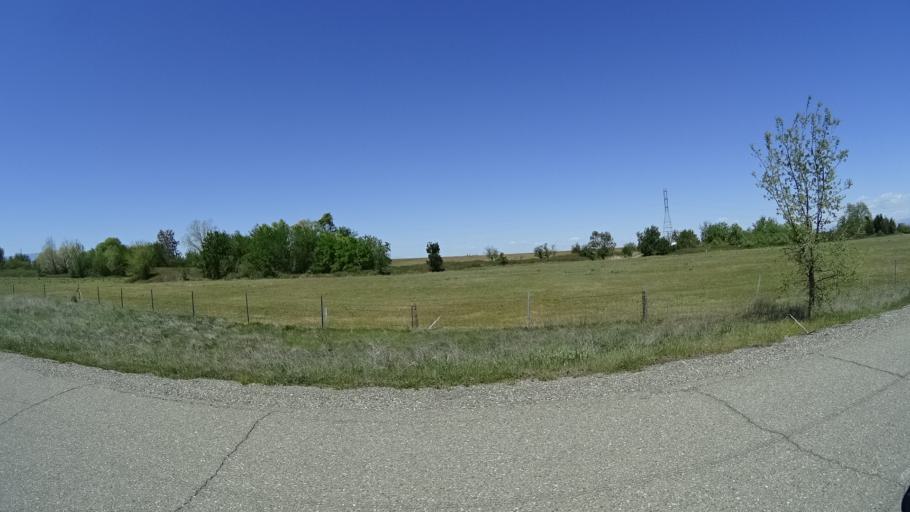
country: US
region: California
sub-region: Glenn County
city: Orland
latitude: 39.7979
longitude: -122.2037
